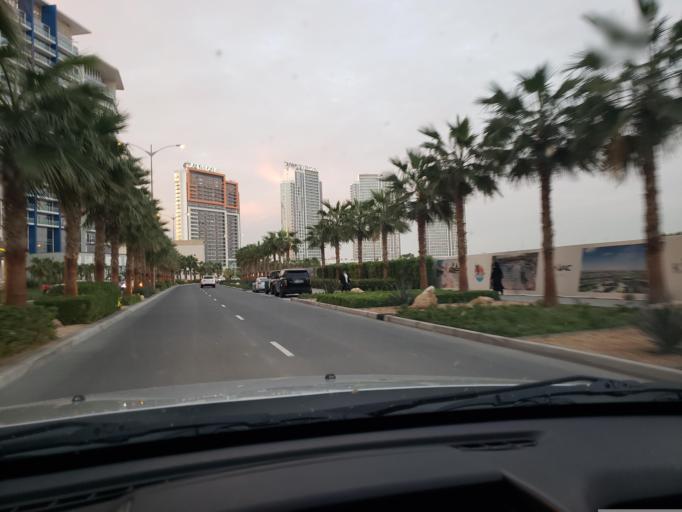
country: AE
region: Dubai
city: Dubai
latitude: 25.0195
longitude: 55.2459
